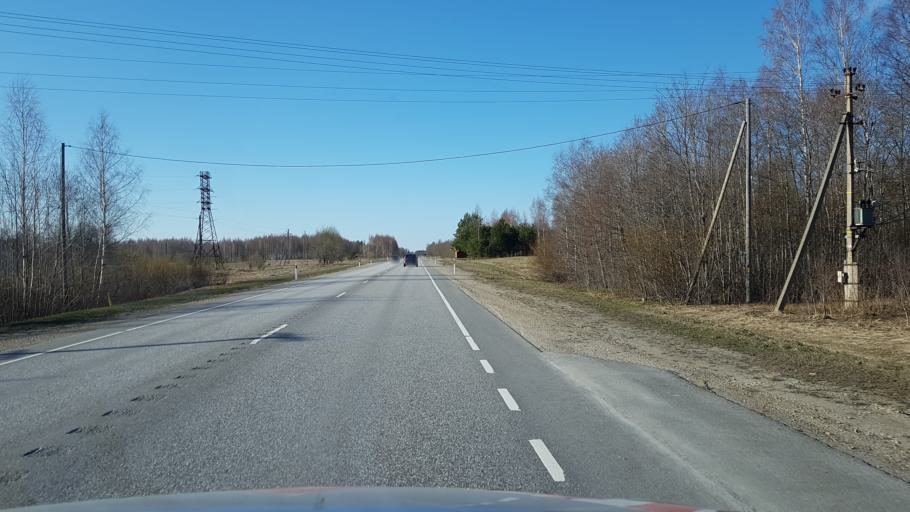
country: EE
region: Ida-Virumaa
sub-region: Johvi vald
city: Johvi
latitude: 59.2092
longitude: 27.3425
